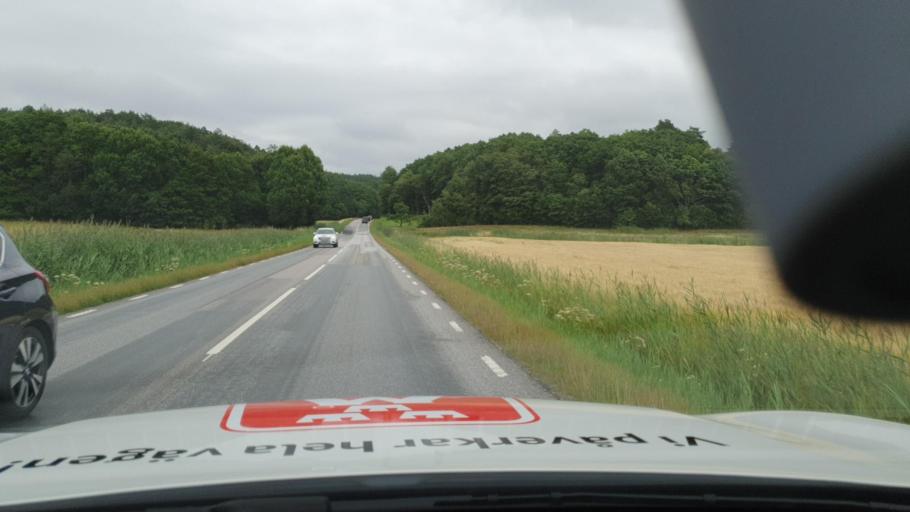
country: SE
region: Vaestra Goetaland
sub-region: Sotenas Kommun
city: Hunnebostrand
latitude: 58.4243
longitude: 11.3920
